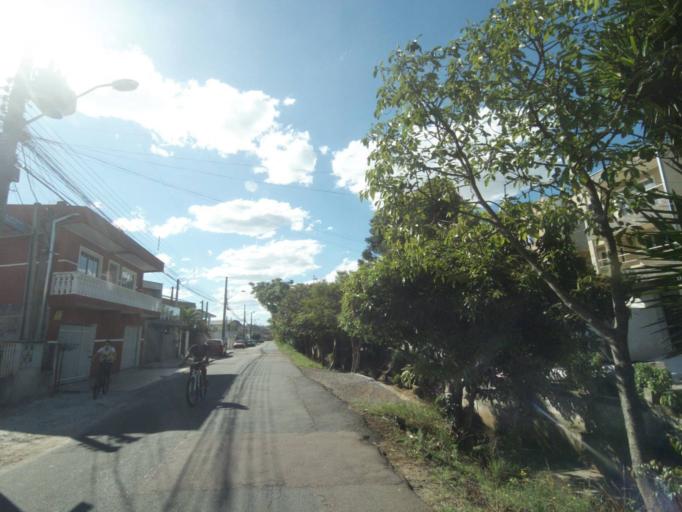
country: BR
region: Parana
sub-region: Curitiba
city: Curitiba
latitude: -25.5116
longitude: -49.3337
